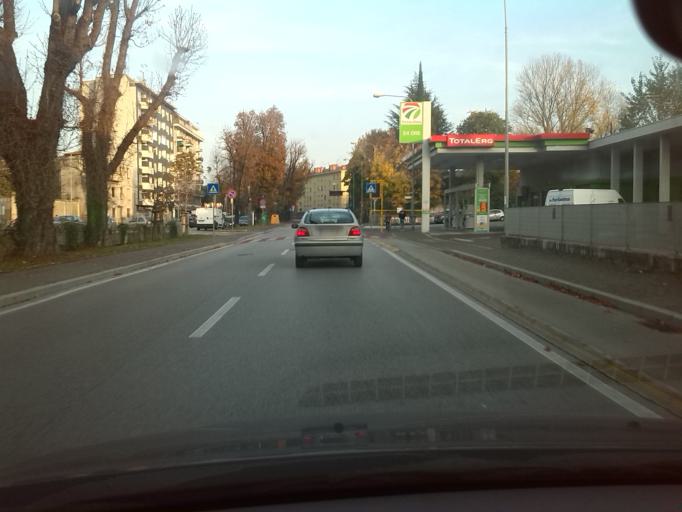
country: IT
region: Friuli Venezia Giulia
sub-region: Provincia di Udine
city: Udine
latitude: 46.0547
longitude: 13.2309
